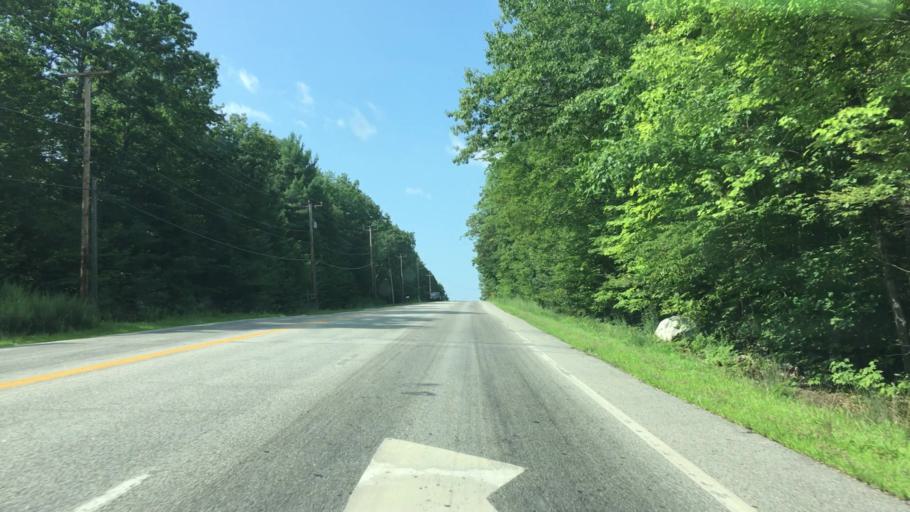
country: US
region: Maine
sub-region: Androscoggin County
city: Poland
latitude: 44.0200
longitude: -70.3551
